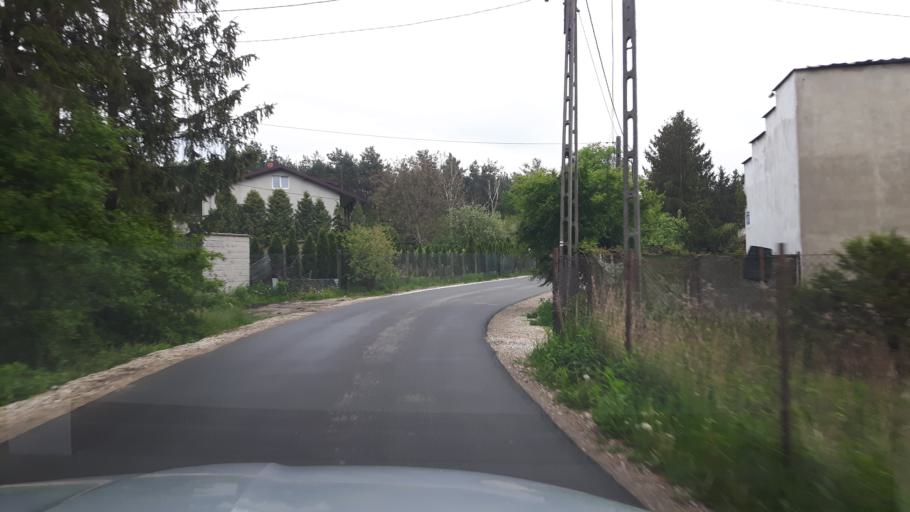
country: PL
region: Masovian Voivodeship
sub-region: Warszawa
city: Rembertow
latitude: 52.2761
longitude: 21.1473
